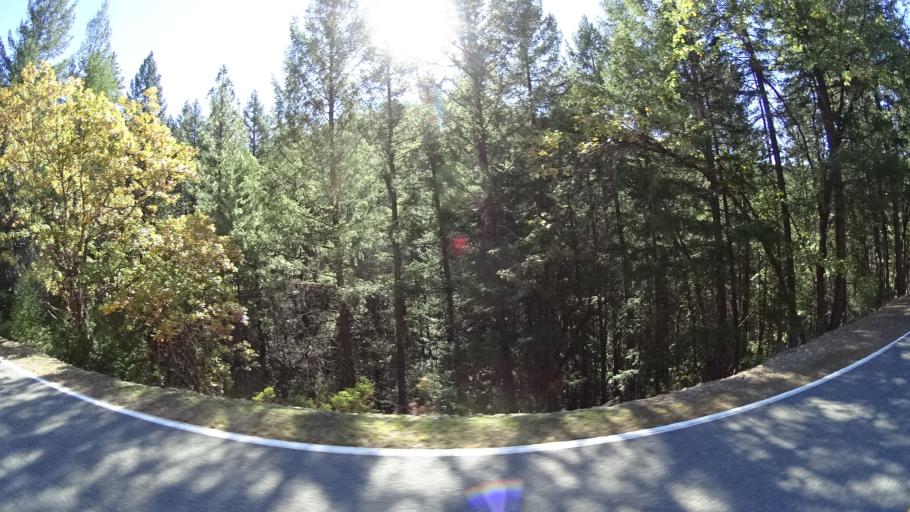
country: US
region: California
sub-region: Trinity County
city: Weaverville
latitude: 41.2030
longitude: -123.0681
